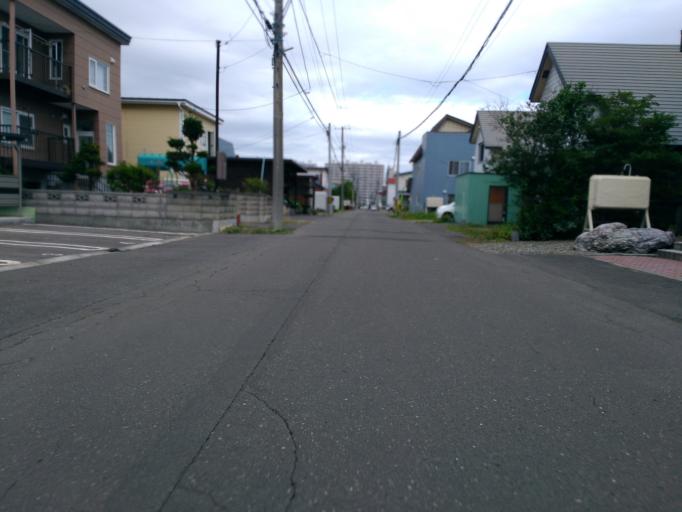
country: JP
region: Hokkaido
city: Ebetsu
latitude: 43.0856
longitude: 141.5267
